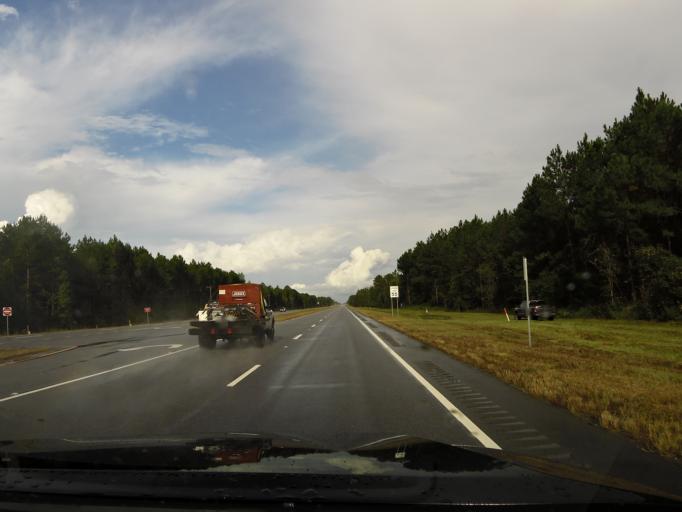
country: US
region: Georgia
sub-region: Liberty County
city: Walthourville
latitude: 31.7449
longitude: -81.6863
